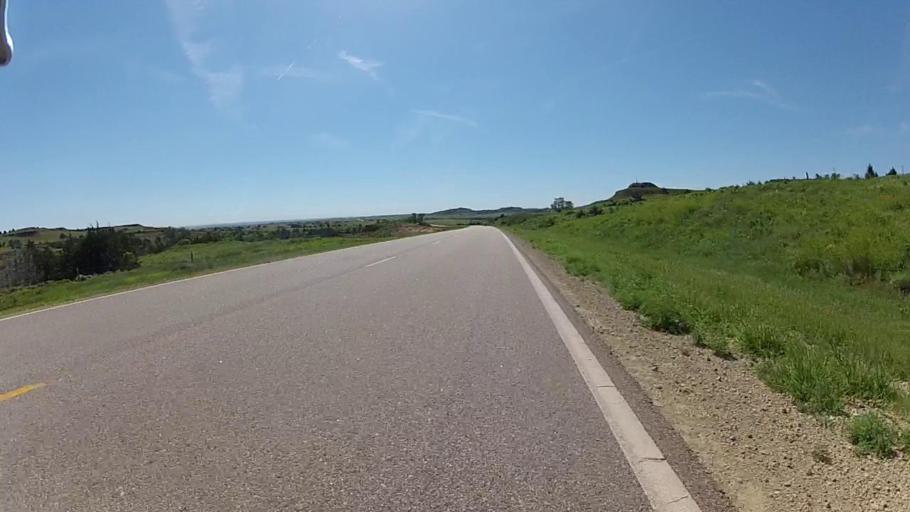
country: US
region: Kansas
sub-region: Barber County
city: Medicine Lodge
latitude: 37.2769
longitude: -98.7351
